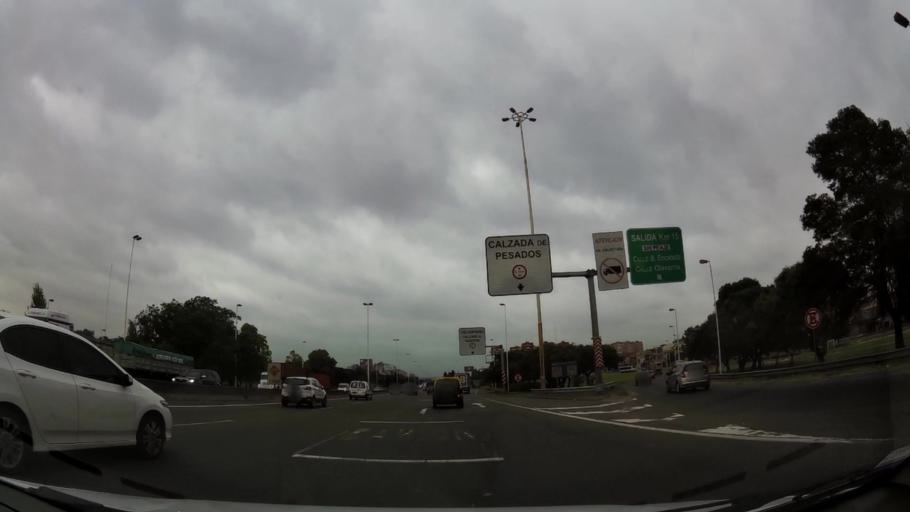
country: AR
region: Buenos Aires F.D.
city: Villa Lugano
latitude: -34.6886
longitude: -58.4869
